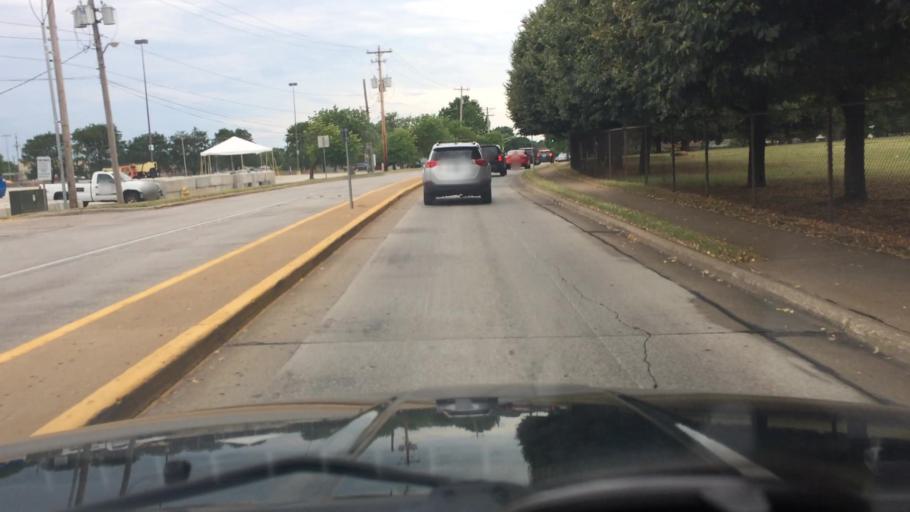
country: US
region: Missouri
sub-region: Greene County
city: Springfield
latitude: 37.1671
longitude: -93.2634
